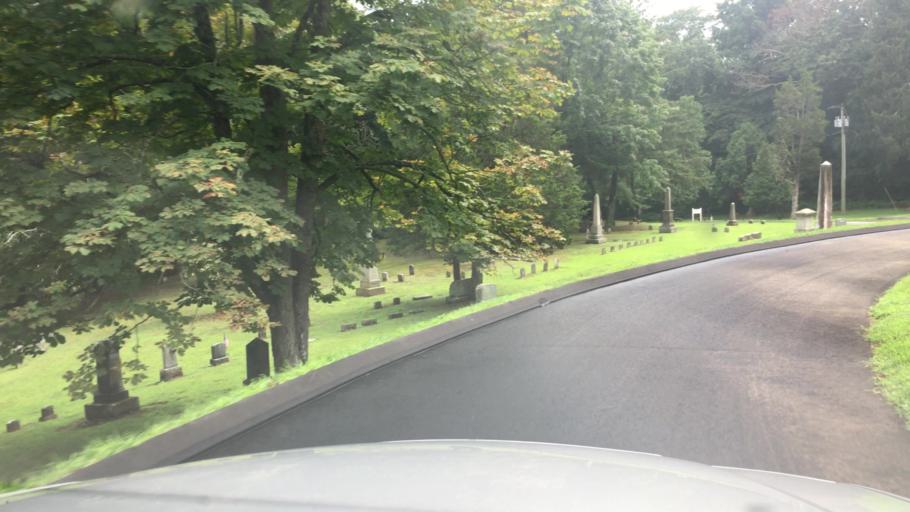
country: US
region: Connecticut
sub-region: Middlesex County
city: Deep River Center
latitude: 41.3848
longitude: -72.4296
